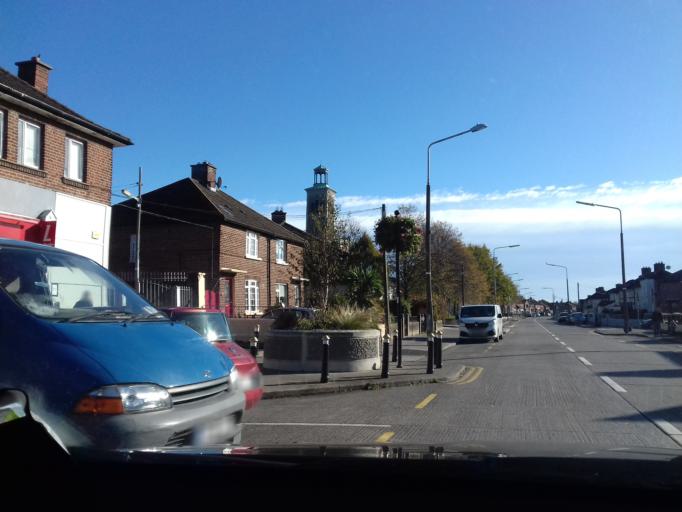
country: IE
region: Leinster
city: Cabra
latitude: 53.3673
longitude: -6.2982
